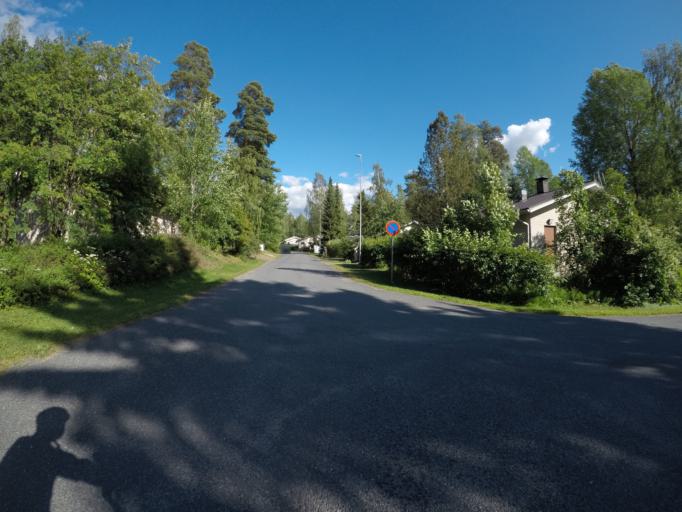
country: FI
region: Haeme
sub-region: Haemeenlinna
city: Haemeenlinna
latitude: 61.0168
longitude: 24.5130
